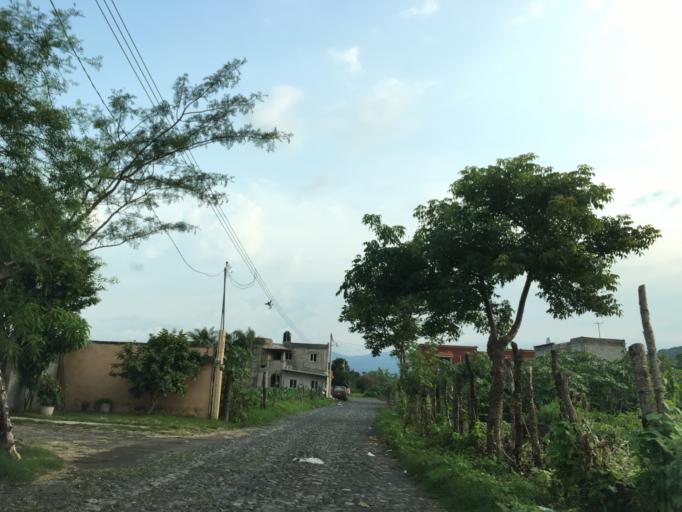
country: MX
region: Nayarit
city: Jala
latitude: 21.0991
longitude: -104.4341
